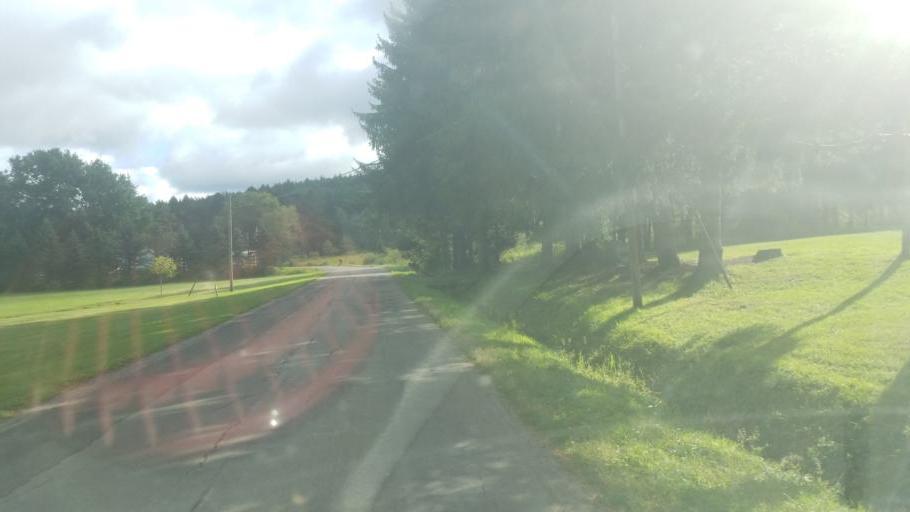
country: US
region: New York
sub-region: Cattaraugus County
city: Weston Mills
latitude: 42.1143
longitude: -78.3189
